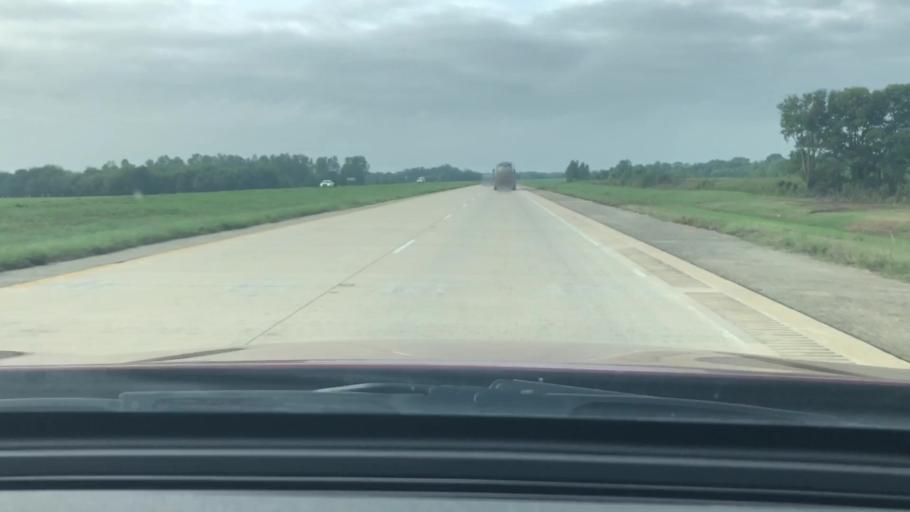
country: US
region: Louisiana
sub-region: Caddo Parish
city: Vivian
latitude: 32.8688
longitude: -93.8605
